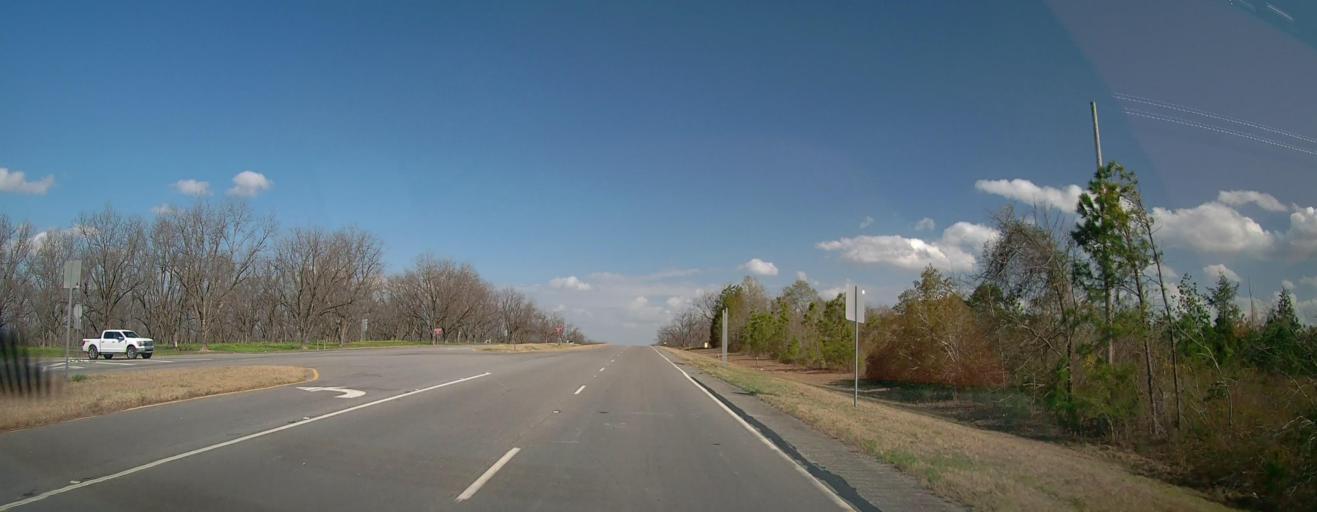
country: US
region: Georgia
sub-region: Dodge County
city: Eastman
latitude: 32.1993
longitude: -83.2347
